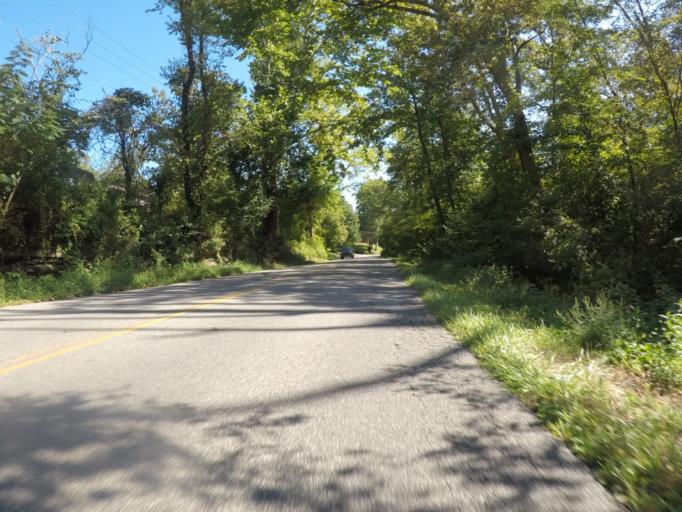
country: US
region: Kentucky
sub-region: Greenup County
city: Russell
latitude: 38.5006
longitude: -82.6961
